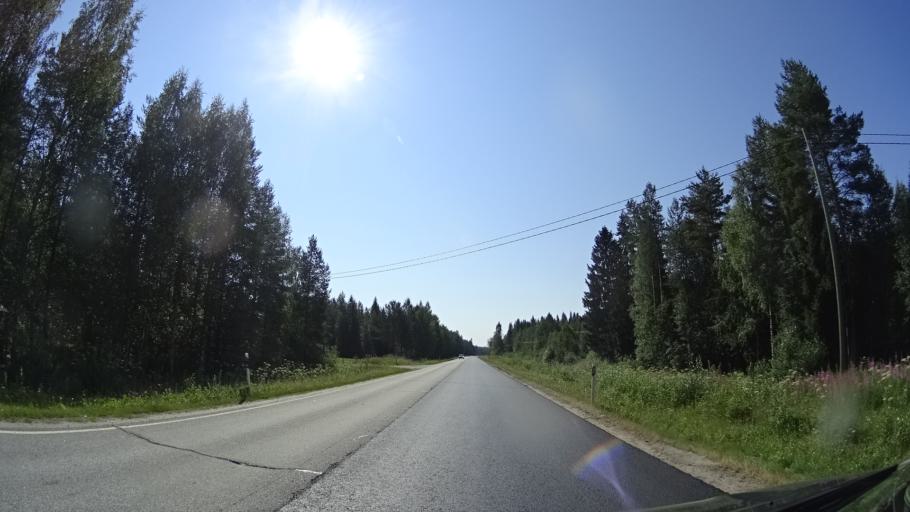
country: FI
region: North Karelia
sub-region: Joensuu
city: Juuka
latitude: 63.2233
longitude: 29.2947
